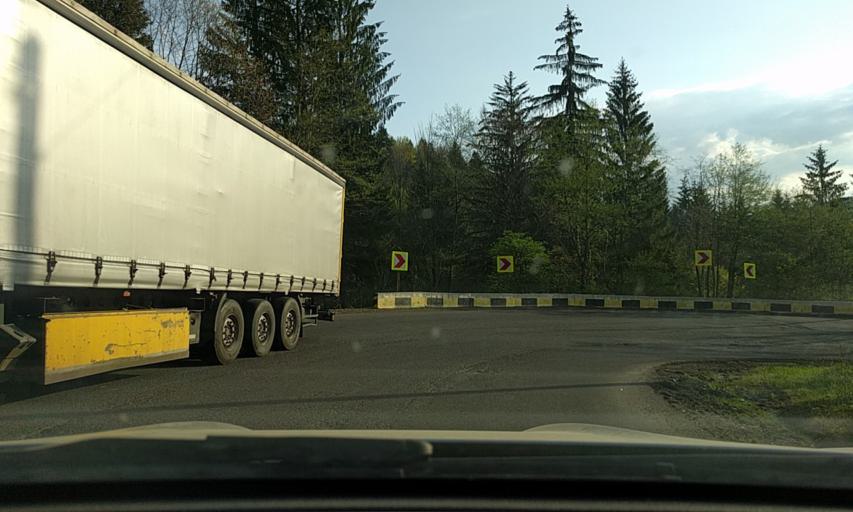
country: RO
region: Covasna
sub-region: Comuna Bretcu
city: Bretcu
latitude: 46.0692
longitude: 26.3832
